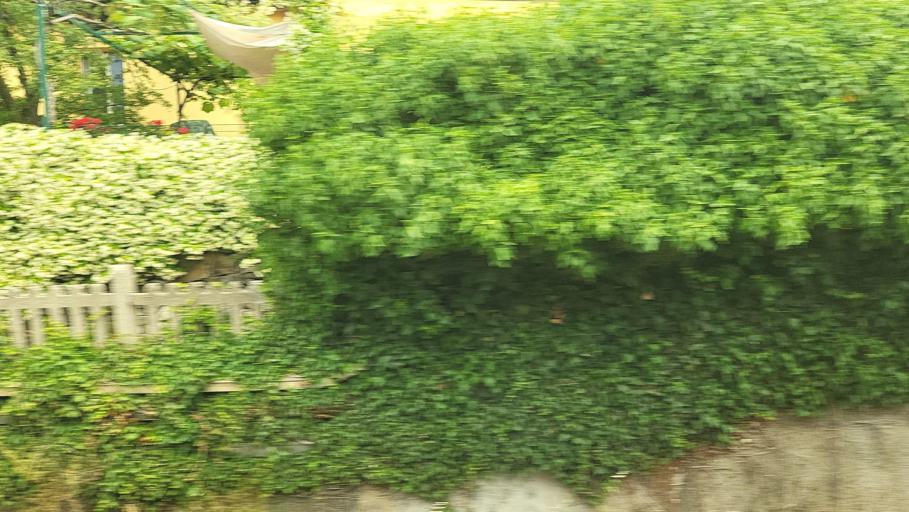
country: IT
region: Friuli Venezia Giulia
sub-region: Provincia di Trieste
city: Villa Opicina
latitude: 45.6819
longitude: 13.7555
